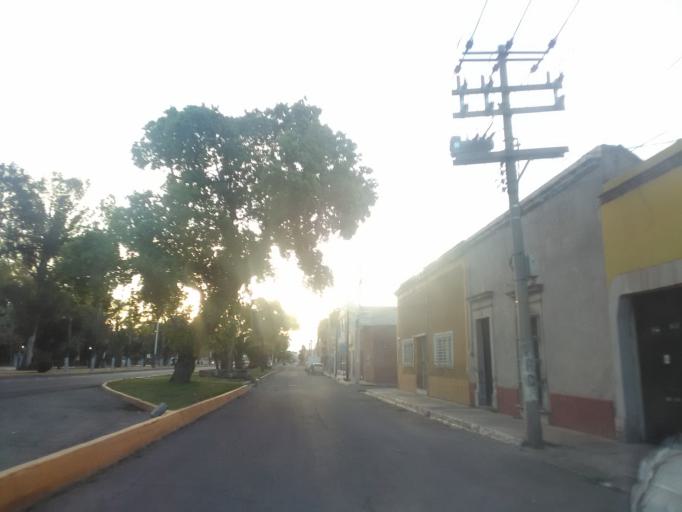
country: MX
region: Durango
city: Victoria de Durango
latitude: 24.0202
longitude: -104.6714
